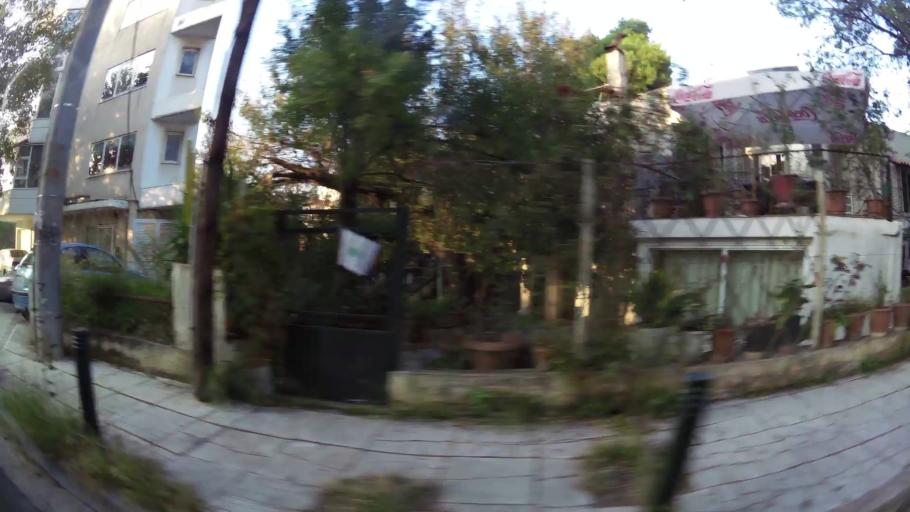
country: GR
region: Attica
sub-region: Nomarchia Athinas
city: Agia Paraskevi
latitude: 38.0162
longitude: 23.8233
